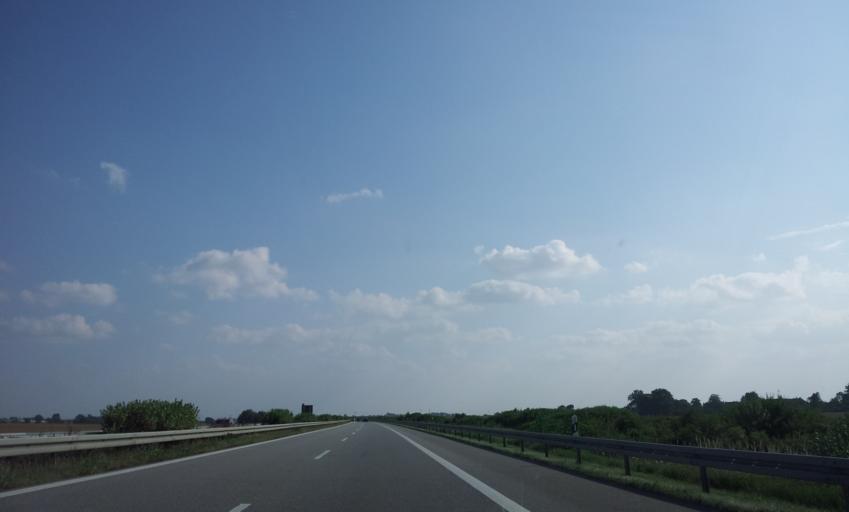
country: DE
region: Mecklenburg-Vorpommern
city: Jarmen
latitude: 53.8497
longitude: 13.3321
